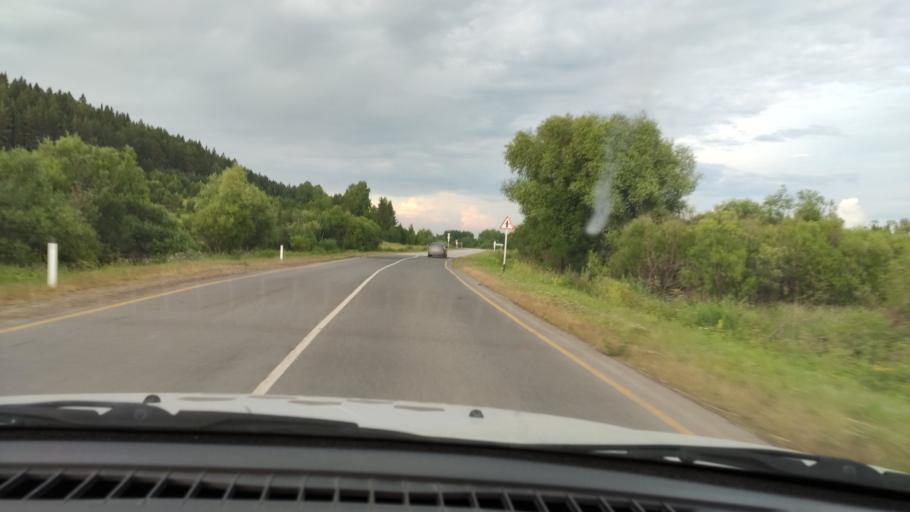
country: RU
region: Perm
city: Kukushtan
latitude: 57.4859
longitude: 56.6105
